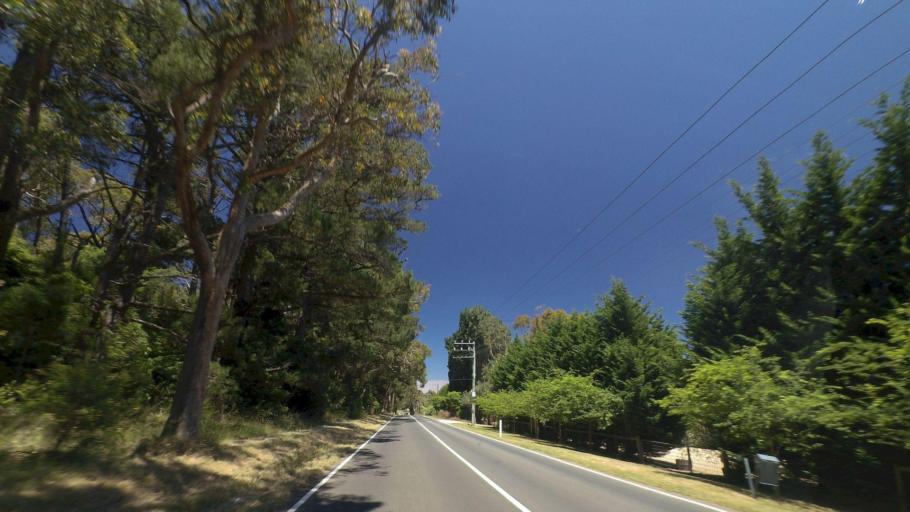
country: AU
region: Victoria
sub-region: Mornington Peninsula
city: Dromana
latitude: -38.3853
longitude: 144.9747
